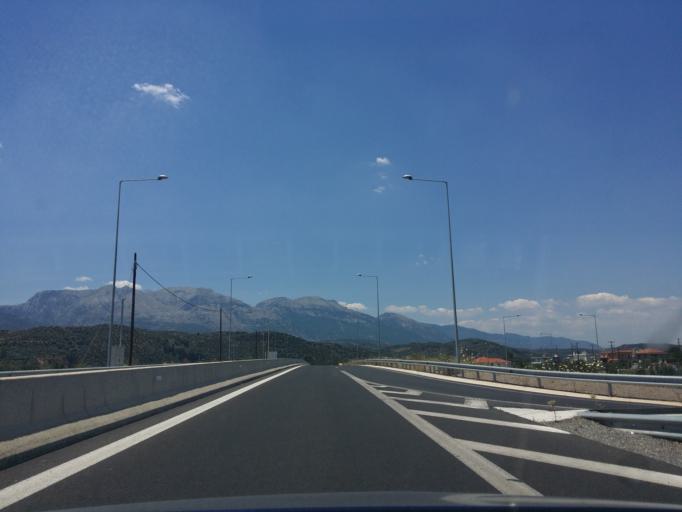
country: GR
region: Peloponnese
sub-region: Nomos Lakonias
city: Sparti
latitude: 37.0935
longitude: 22.4341
